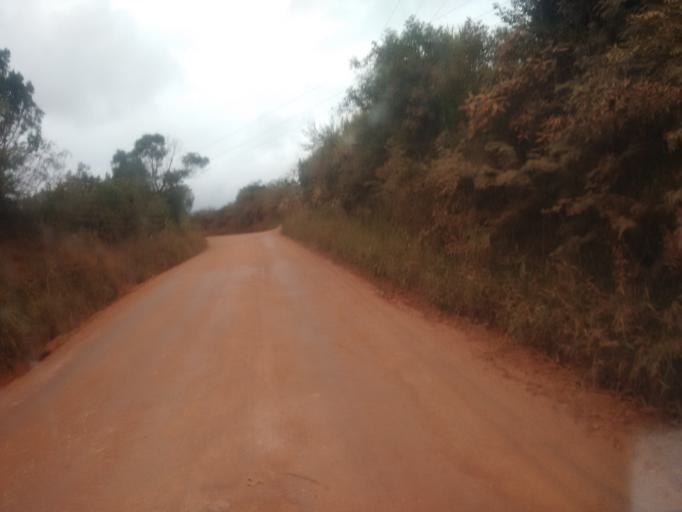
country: BR
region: Rio Grande do Sul
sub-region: Camaqua
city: Camaqua
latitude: -30.8204
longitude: -51.8142
